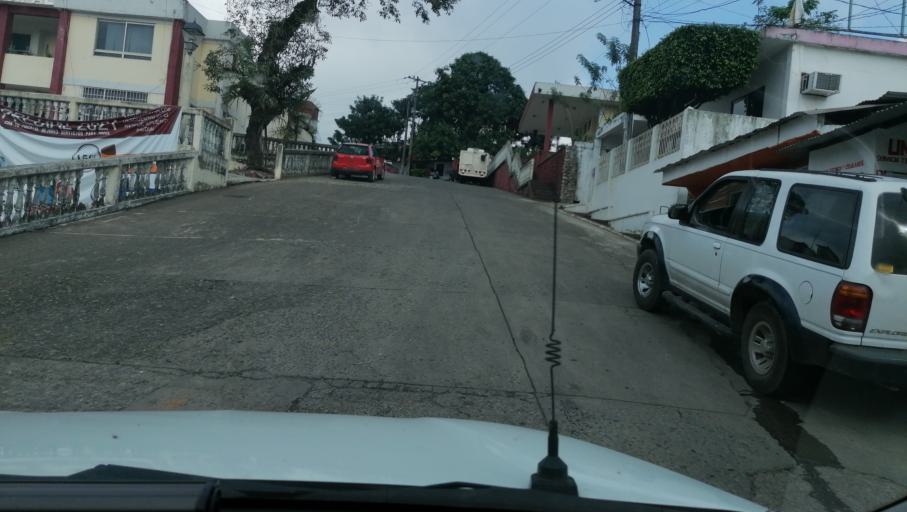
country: MX
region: Chiapas
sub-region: Juarez
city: El Triunfo 1ra. Seccion (Cardona)
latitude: 17.6081
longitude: -93.1930
